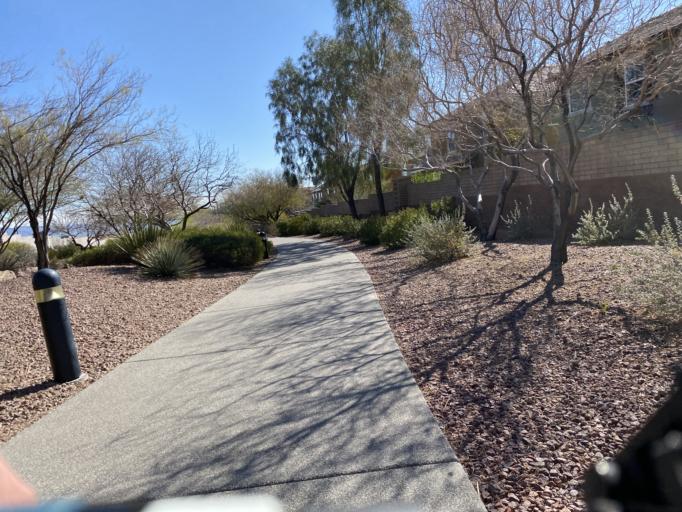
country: US
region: Nevada
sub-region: Clark County
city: Summerlin South
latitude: 36.2919
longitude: -115.3280
